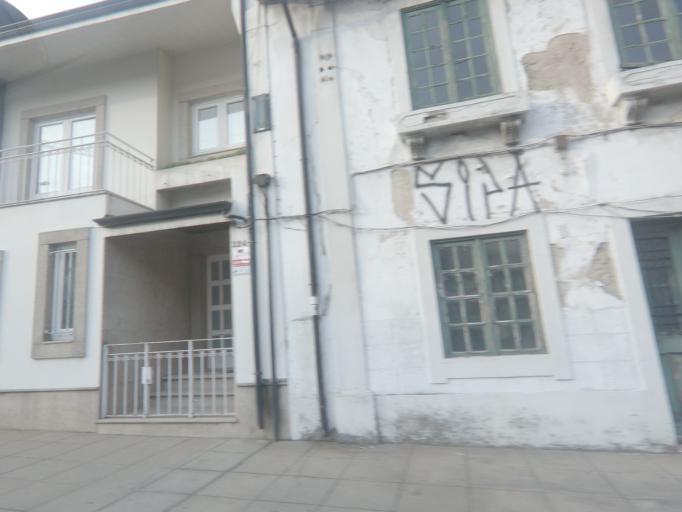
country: PT
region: Porto
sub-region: Valongo
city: Valongo
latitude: 41.1885
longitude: -8.4937
